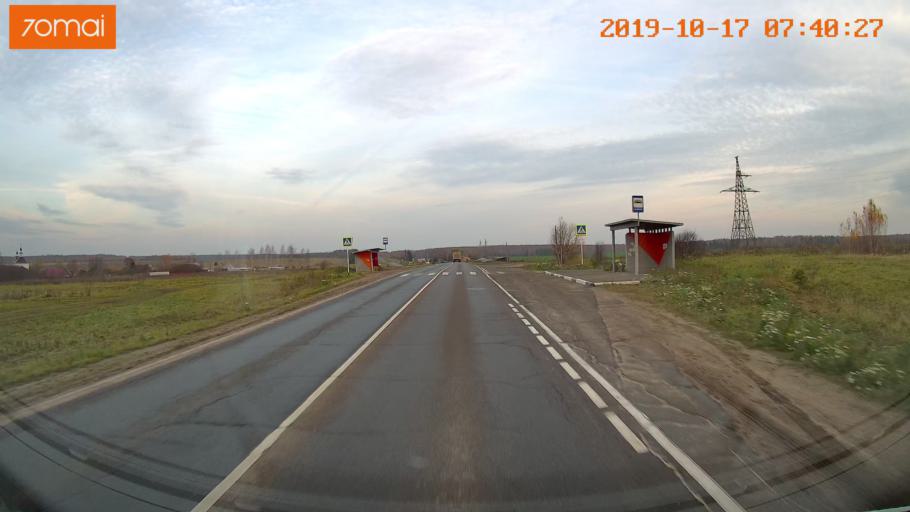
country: RU
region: Vladimir
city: Yur'yev-Pol'skiy
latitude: 56.4728
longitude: 39.8299
